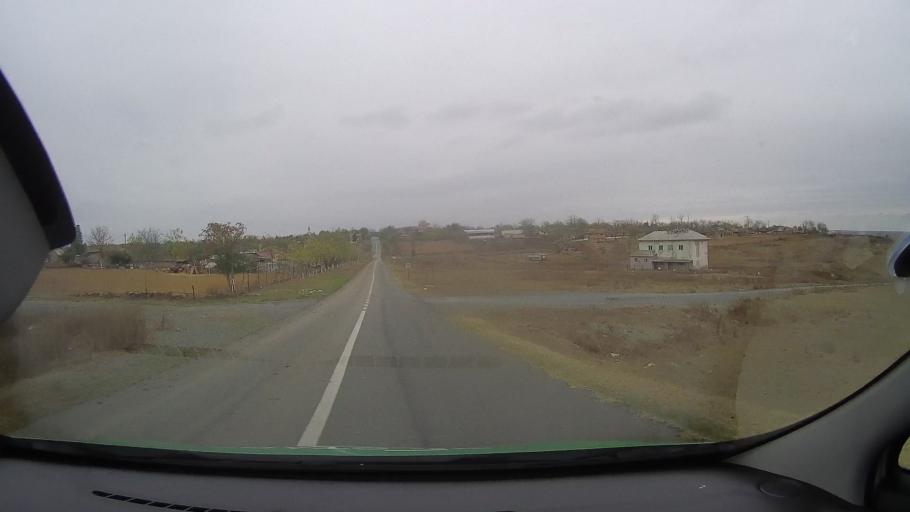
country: RO
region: Constanta
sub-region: Comuna Pantelimon
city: Pantelimon
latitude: 44.5405
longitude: 28.3292
